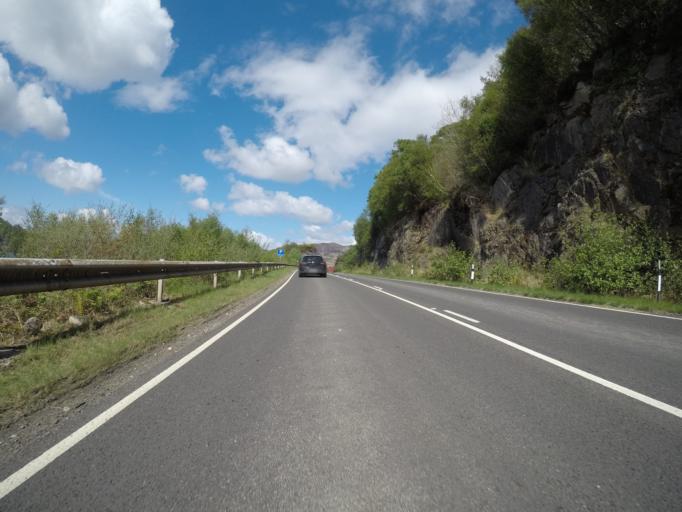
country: GB
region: Scotland
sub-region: Highland
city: Fort William
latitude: 57.2695
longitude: -5.5075
